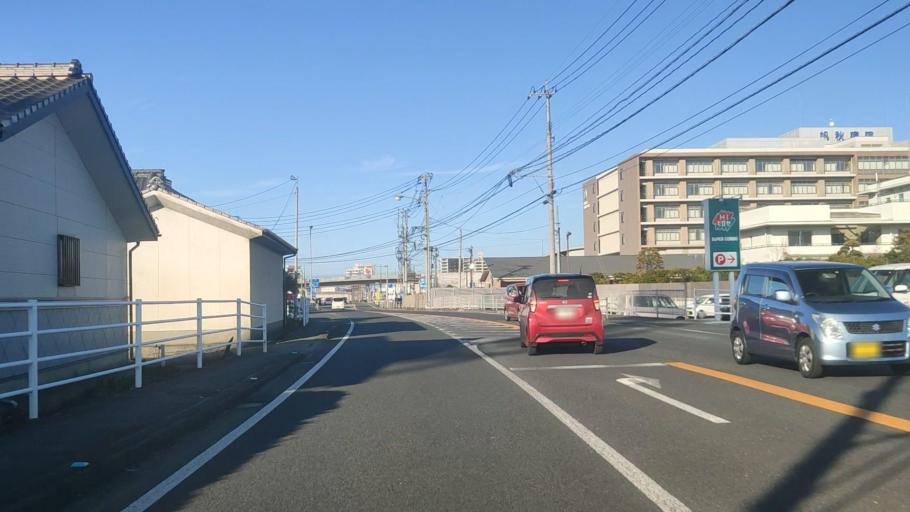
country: JP
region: Oita
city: Oita
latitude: 33.2235
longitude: 131.6186
